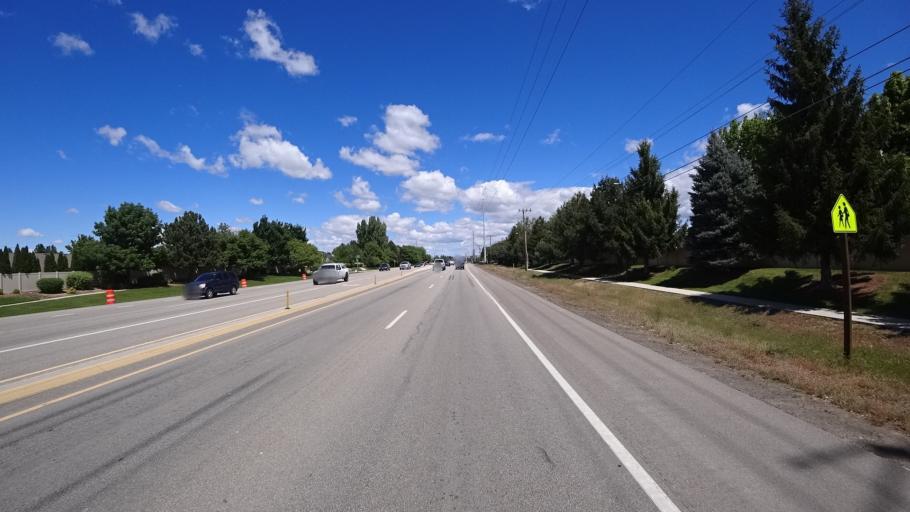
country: US
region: Idaho
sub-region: Ada County
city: Meridian
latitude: 43.6449
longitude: -116.3543
